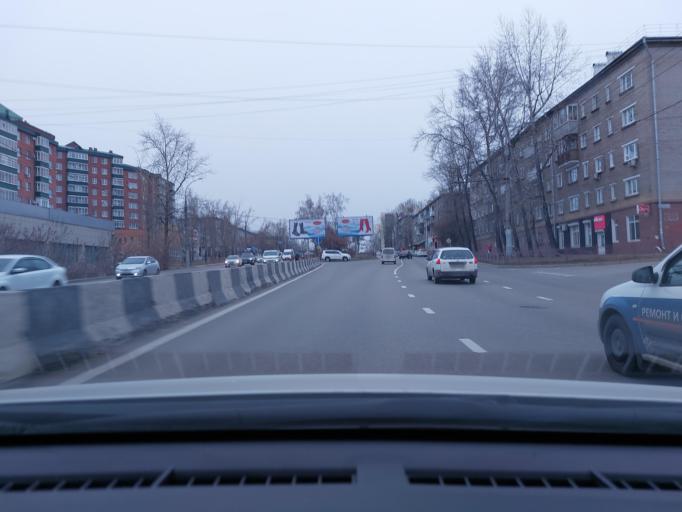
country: RU
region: Irkutsk
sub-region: Irkutskiy Rayon
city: Irkutsk
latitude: 52.2658
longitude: 104.2584
